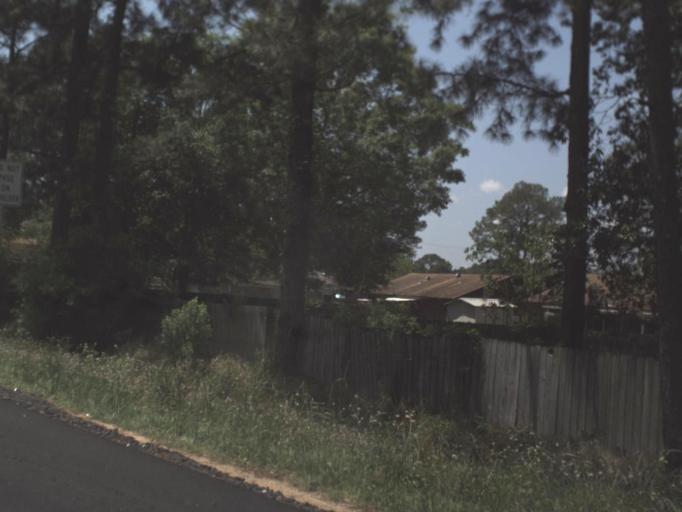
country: US
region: Florida
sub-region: Escambia County
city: Myrtle Grove
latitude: 30.4260
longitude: -87.3167
